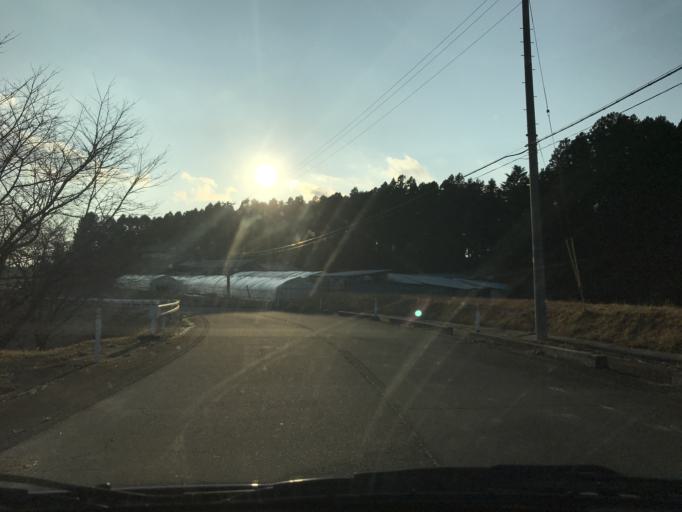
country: JP
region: Miyagi
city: Wakuya
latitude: 38.6828
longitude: 141.1124
